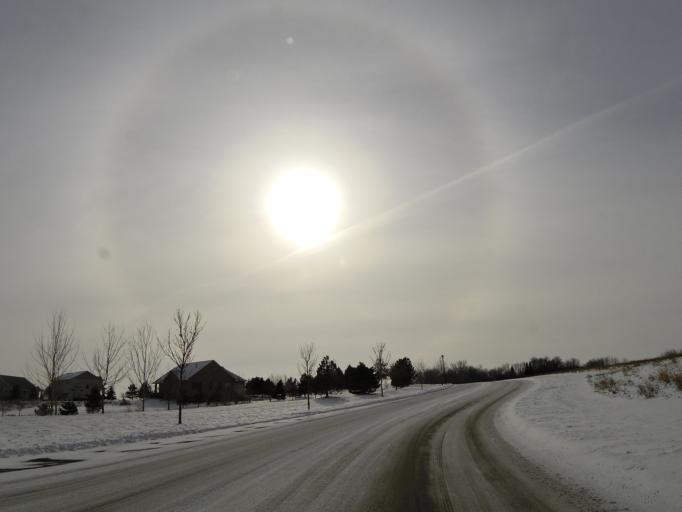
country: US
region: Minnesota
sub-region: Carver County
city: Mayer
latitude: 44.8936
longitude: -93.8784
